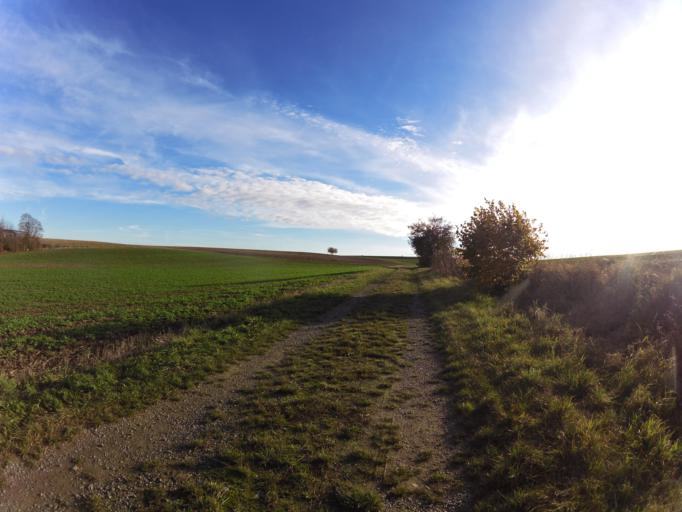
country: DE
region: Bavaria
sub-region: Regierungsbezirk Unterfranken
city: Giebelstadt
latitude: 49.6665
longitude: 9.9564
